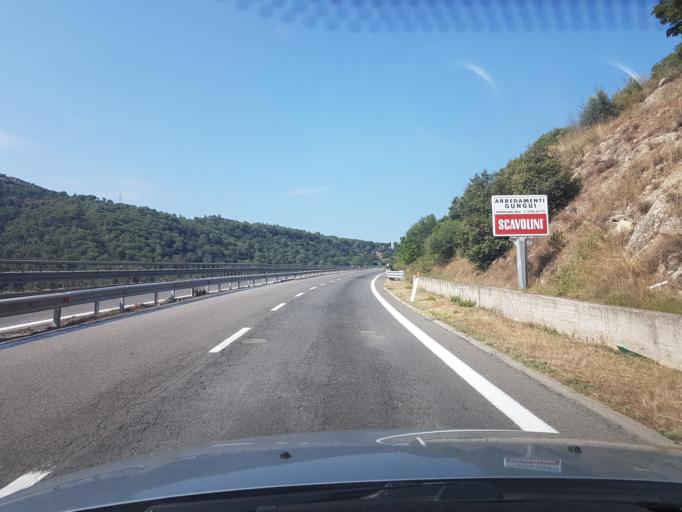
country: IT
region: Sardinia
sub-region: Provincia di Nuoro
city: Nuoro
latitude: 40.3352
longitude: 9.2986
